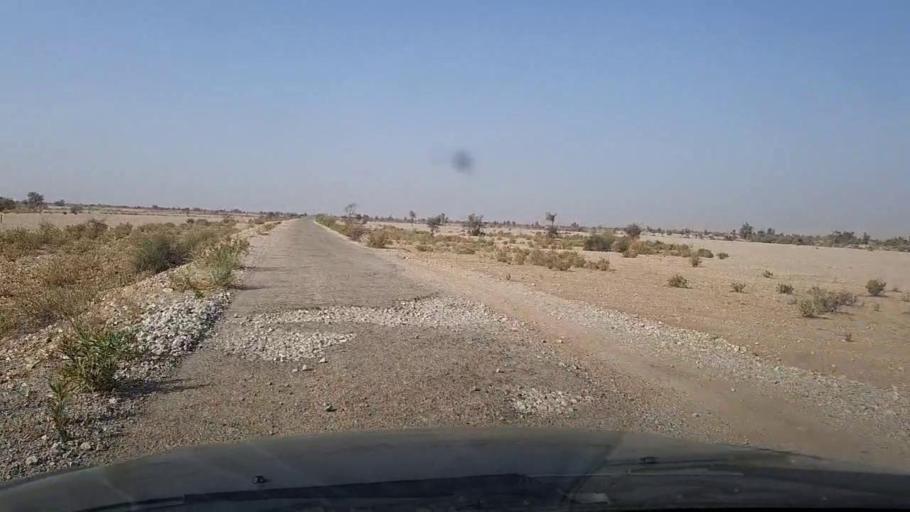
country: PK
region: Sindh
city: Sann
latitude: 25.9213
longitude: 68.0155
